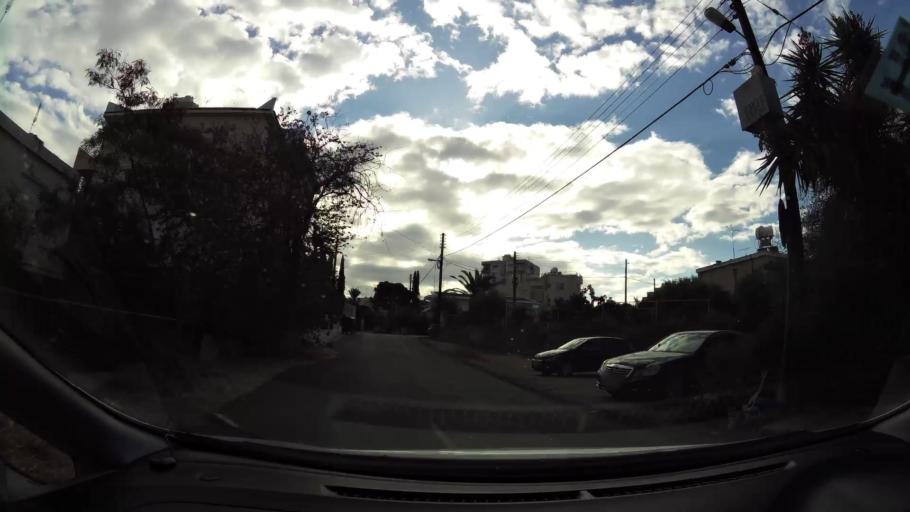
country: CY
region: Lefkosia
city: Nicosia
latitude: 35.1484
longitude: 33.3564
